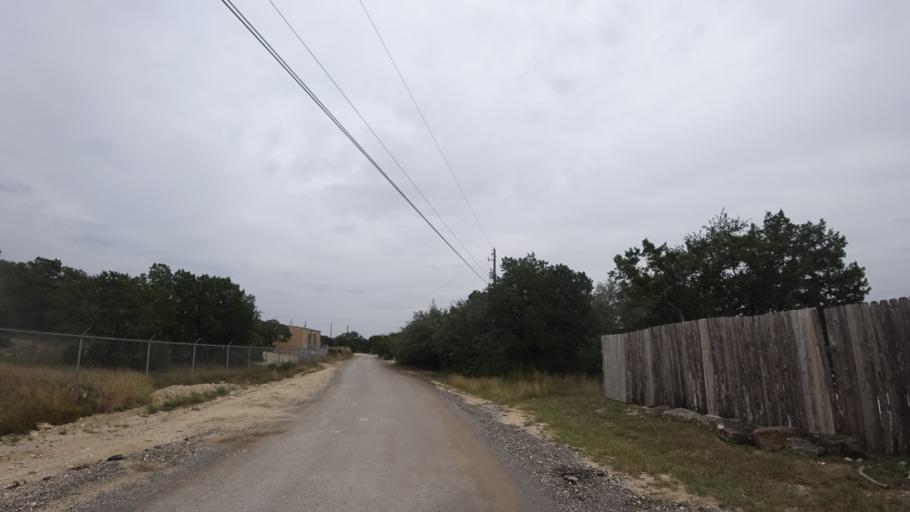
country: US
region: Texas
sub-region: Travis County
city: Hudson Bend
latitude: 30.3810
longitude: -97.9384
